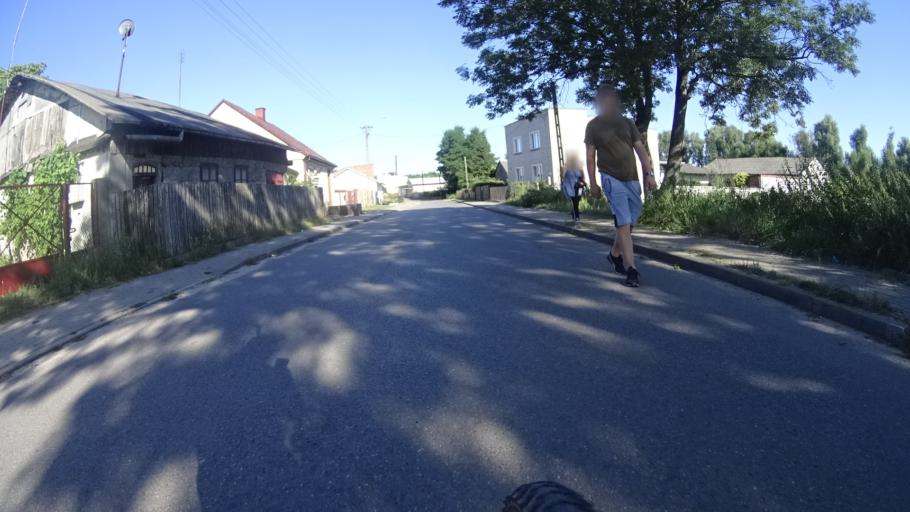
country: PL
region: Masovian Voivodeship
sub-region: Powiat bialobrzeski
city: Wysmierzyce
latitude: 51.6626
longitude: 20.8603
